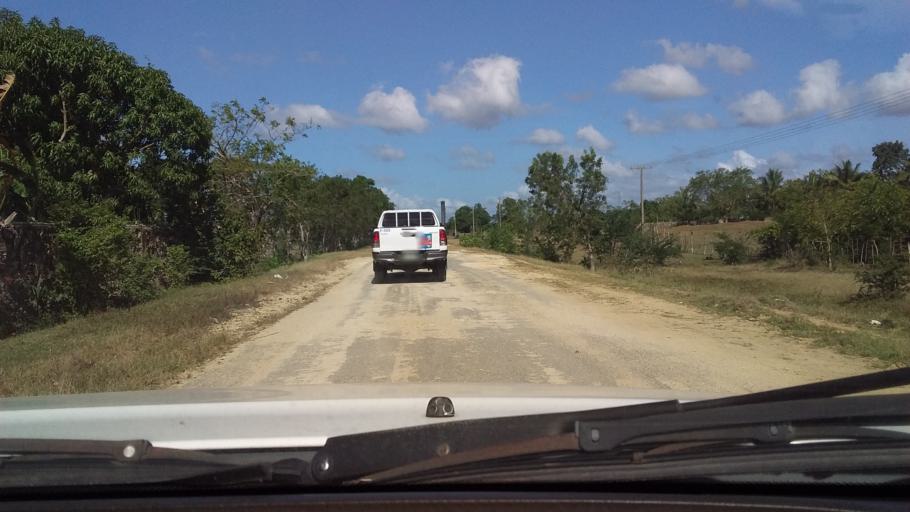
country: DO
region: Santo Domingo
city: Guerra
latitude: 18.5660
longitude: -69.7812
